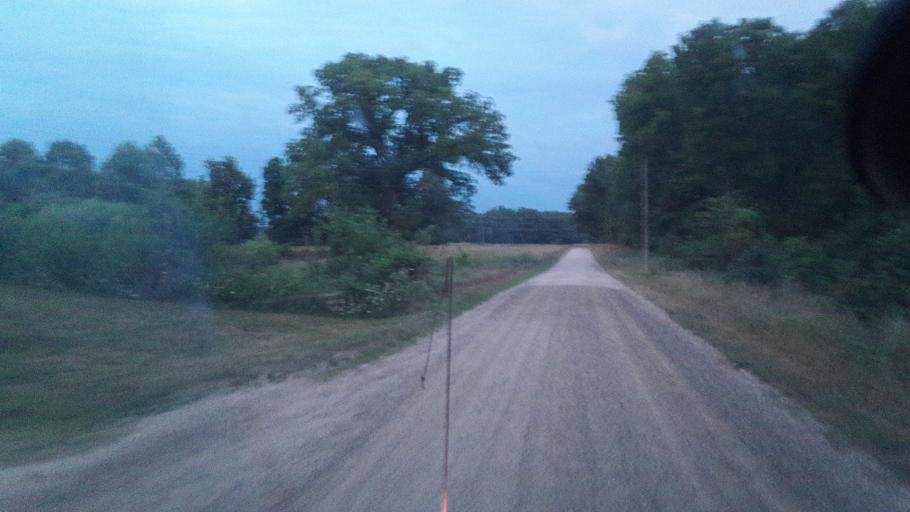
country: US
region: Indiana
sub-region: DeKalb County
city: Butler
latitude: 41.3557
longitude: -84.8288
